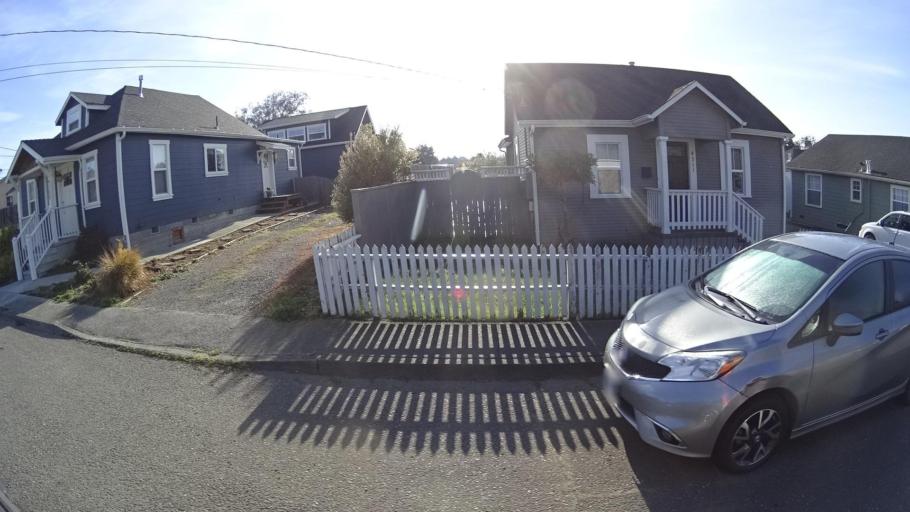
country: US
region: California
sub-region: Humboldt County
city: Bayview
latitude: 40.7683
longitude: -124.1820
